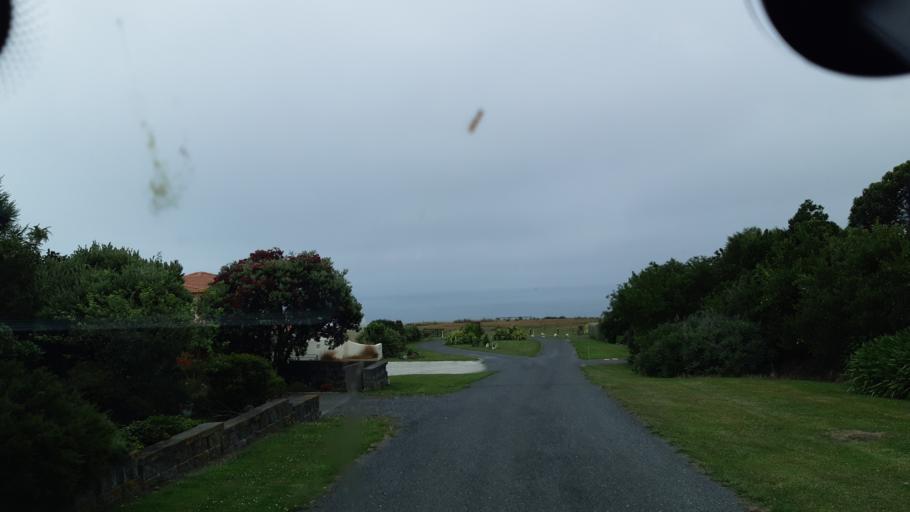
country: NZ
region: Canterbury
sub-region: Kaikoura District
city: Kaikoura
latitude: -42.4176
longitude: 173.6983
